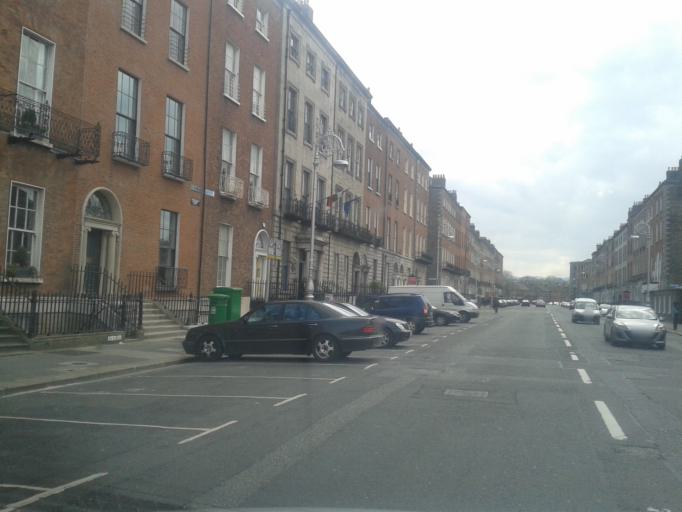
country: IE
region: Leinster
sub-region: Dublin City
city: Dublin
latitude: 53.3347
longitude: -6.2512
